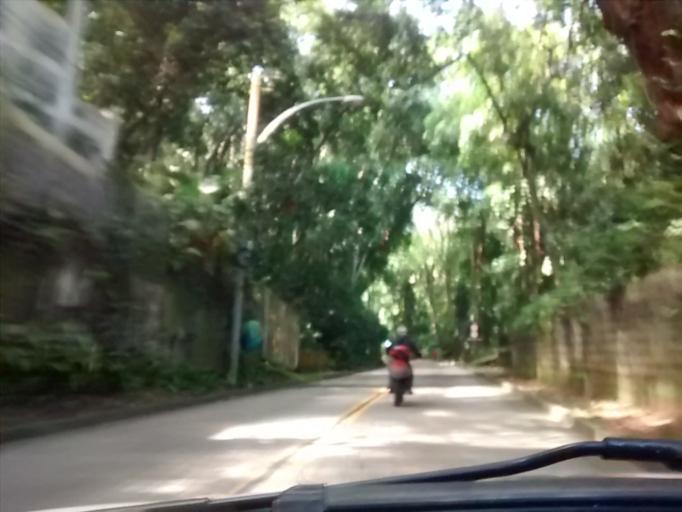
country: BR
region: Rio de Janeiro
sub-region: Rio De Janeiro
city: Rio de Janeiro
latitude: -22.9900
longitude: -43.2743
